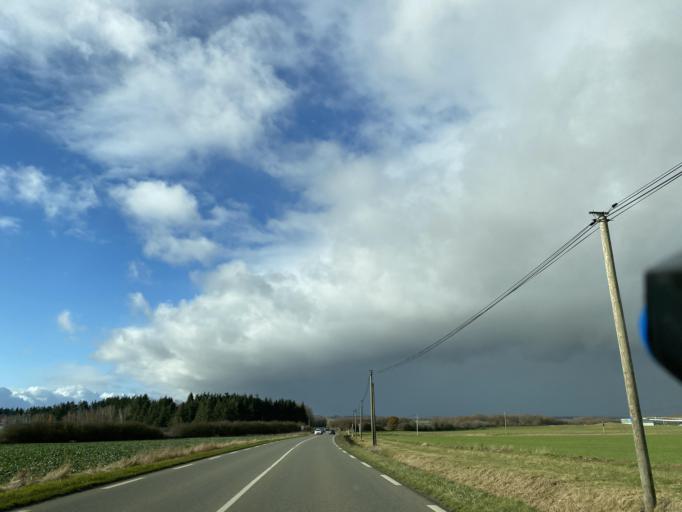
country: FR
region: Centre
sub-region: Departement d'Eure-et-Loir
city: Mainvilliers
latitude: 48.4630
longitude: 1.4324
